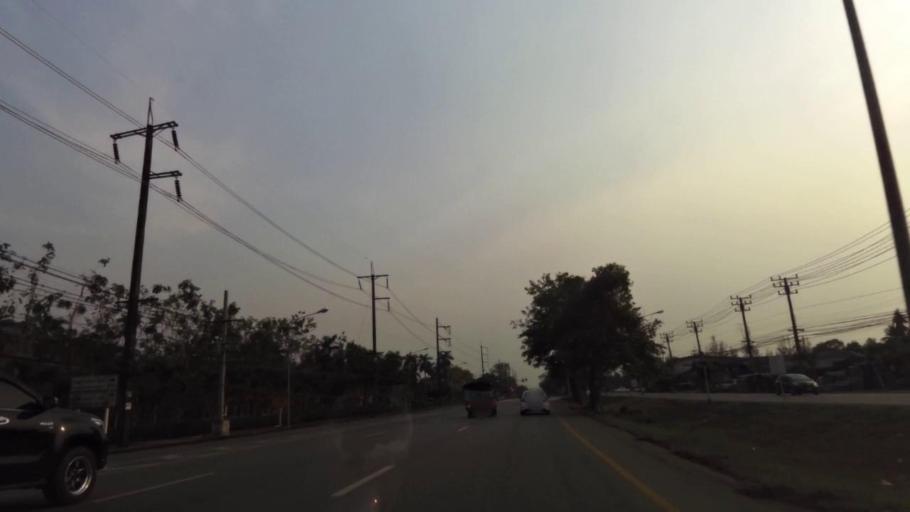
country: TH
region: Chanthaburi
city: Khlung
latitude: 12.5121
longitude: 102.1690
